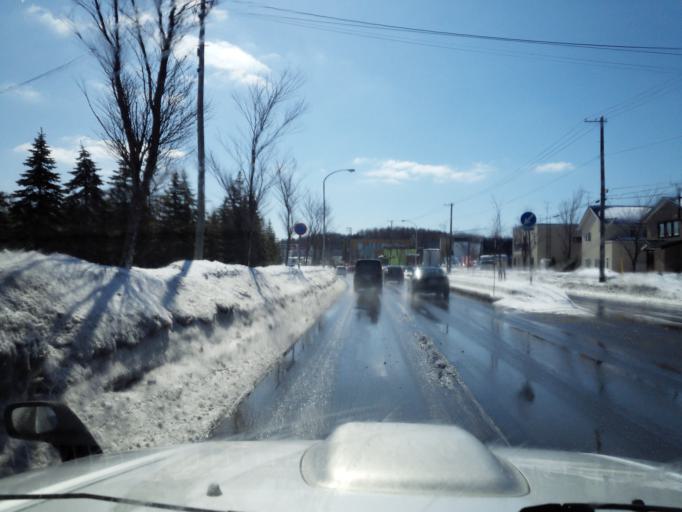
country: JP
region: Hokkaido
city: Kitahiroshima
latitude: 43.0043
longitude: 141.4604
